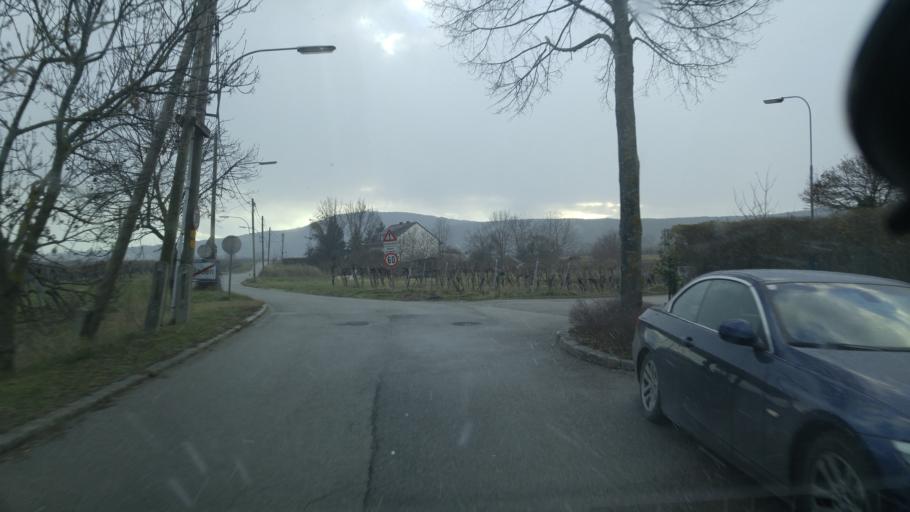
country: AT
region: Lower Austria
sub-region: Politischer Bezirk Baden
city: Baden
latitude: 47.9943
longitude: 16.2092
